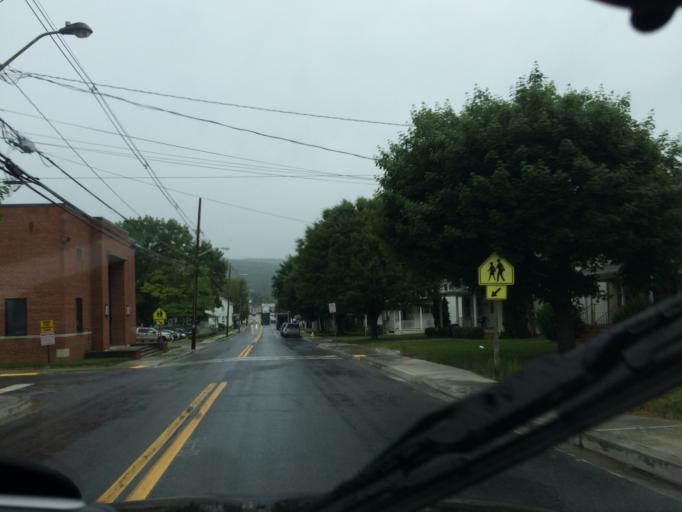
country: US
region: Maryland
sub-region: Frederick County
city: Thurmont
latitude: 39.6208
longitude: -77.4032
